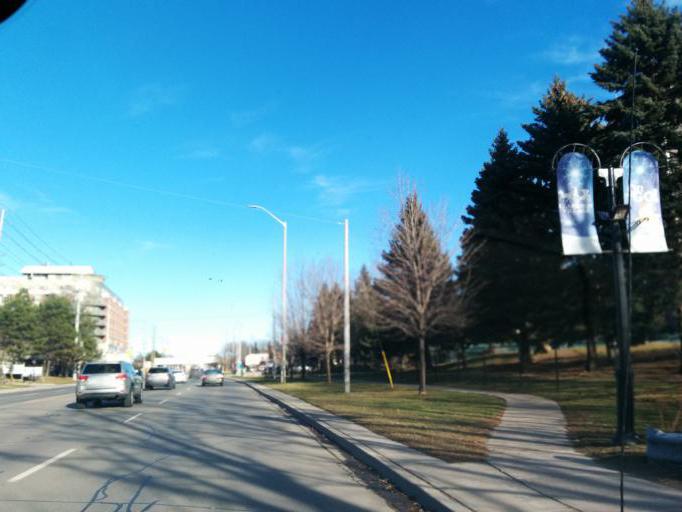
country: CA
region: Ontario
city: Mississauga
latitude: 43.5124
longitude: -79.6284
